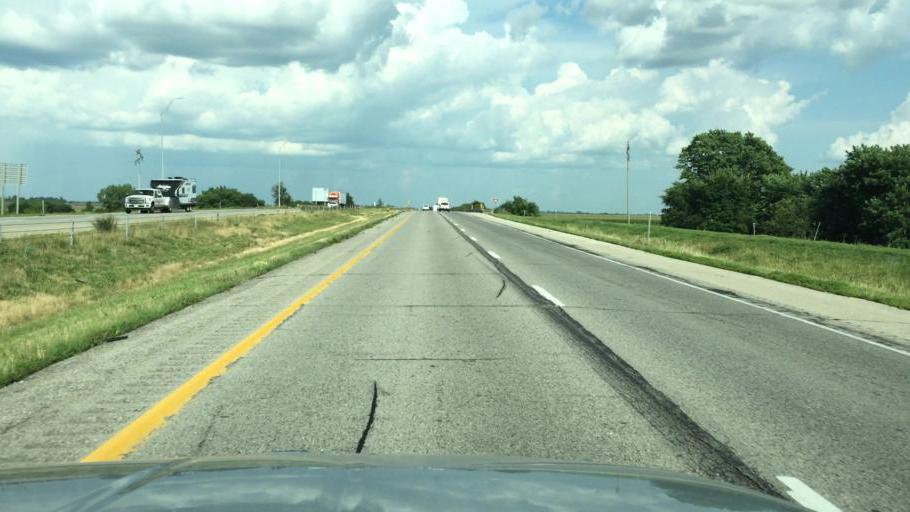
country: US
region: Iowa
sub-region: Poweshiek County
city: Grinnell
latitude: 41.6960
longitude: -92.7238
